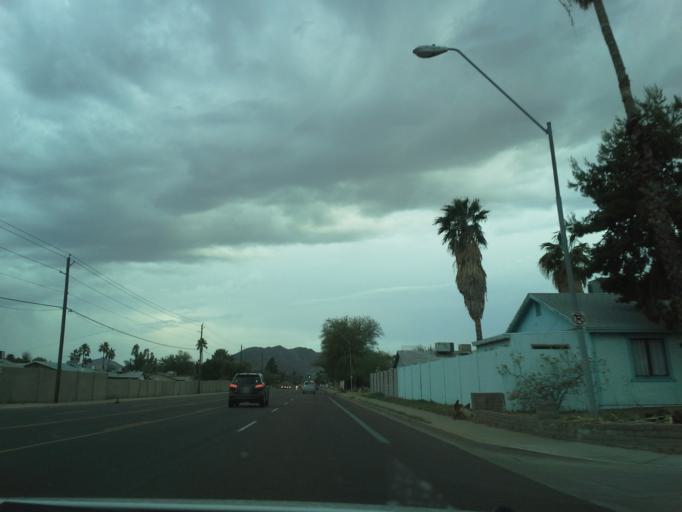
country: US
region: Arizona
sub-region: Maricopa County
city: Paradise Valley
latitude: 33.6075
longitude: -111.9960
